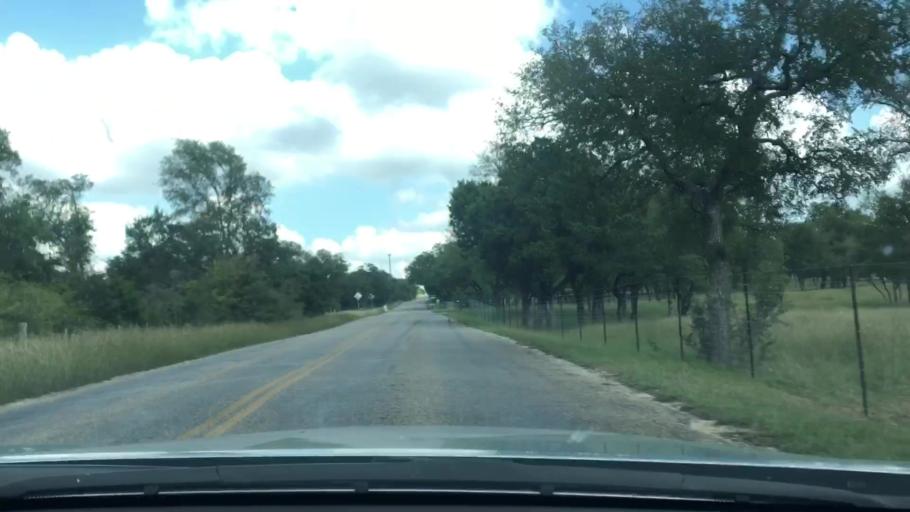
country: US
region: Texas
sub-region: Bexar County
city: Fair Oaks Ranch
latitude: 29.7855
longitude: -98.6458
